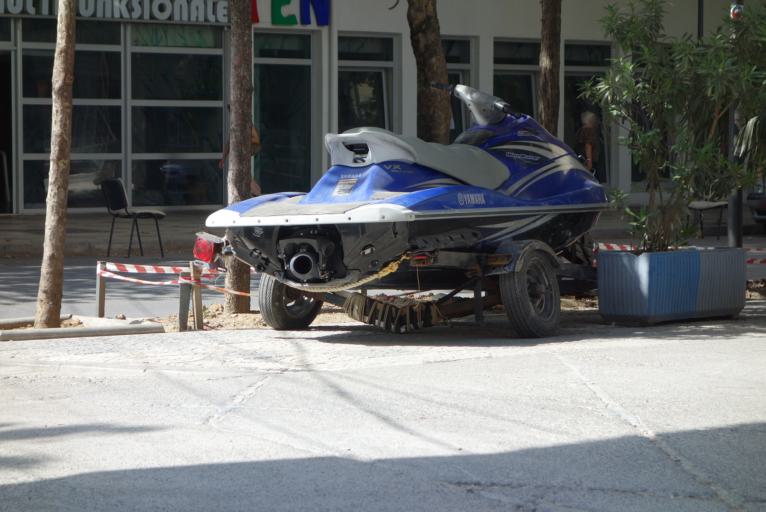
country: AL
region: Tirane
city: Tirana
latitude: 41.3246
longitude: 19.8098
